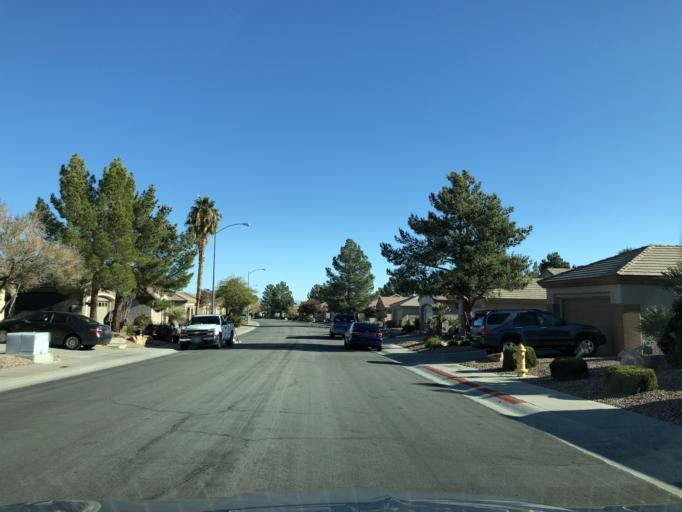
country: US
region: Nevada
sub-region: Clark County
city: Whitney
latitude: 36.0091
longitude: -115.0739
